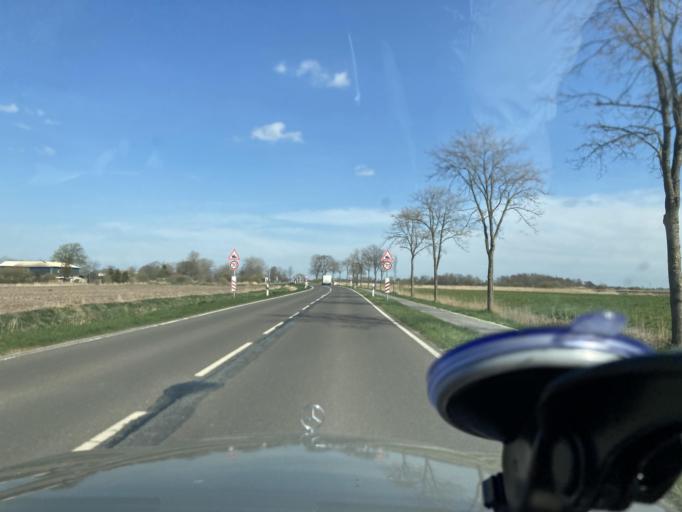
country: DE
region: Schleswig-Holstein
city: Lehe
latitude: 54.3444
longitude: 9.0400
